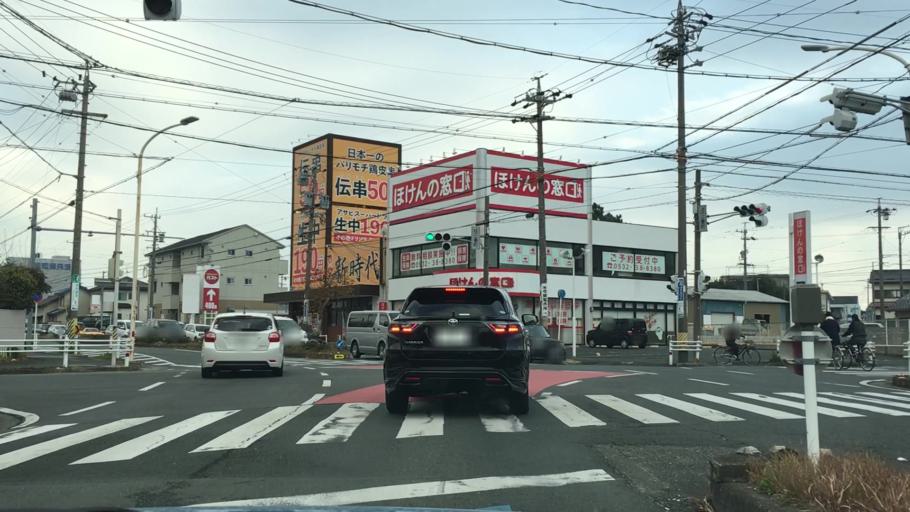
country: JP
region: Aichi
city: Toyohashi
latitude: 34.7495
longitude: 137.3763
